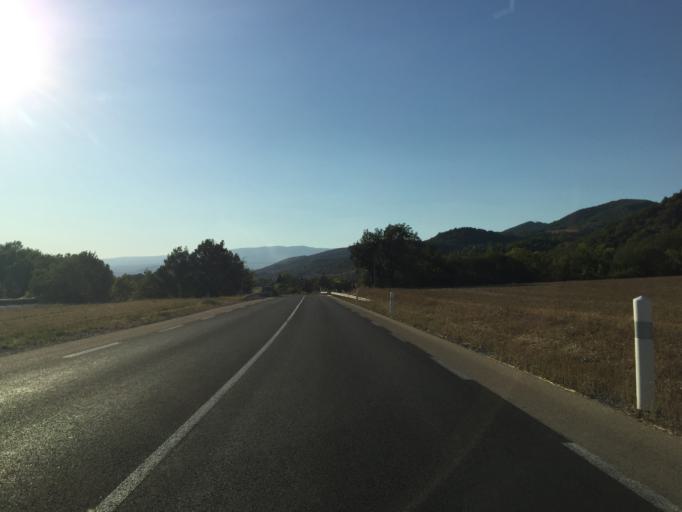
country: FR
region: Provence-Alpes-Cote d'Azur
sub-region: Departement des Alpes-de-Haute-Provence
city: Malijai
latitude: 44.0396
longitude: 6.0758
